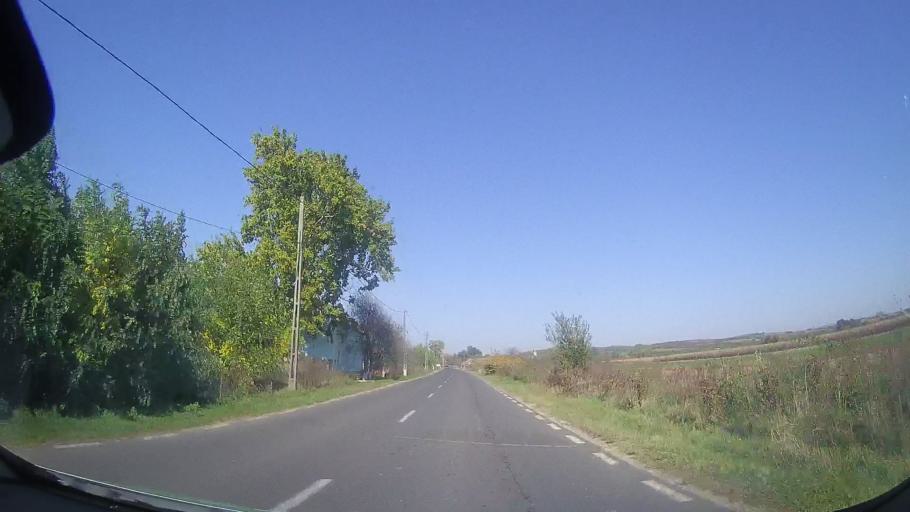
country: RO
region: Timis
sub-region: Comuna Balint
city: Balint
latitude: 45.8062
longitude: 21.8608
